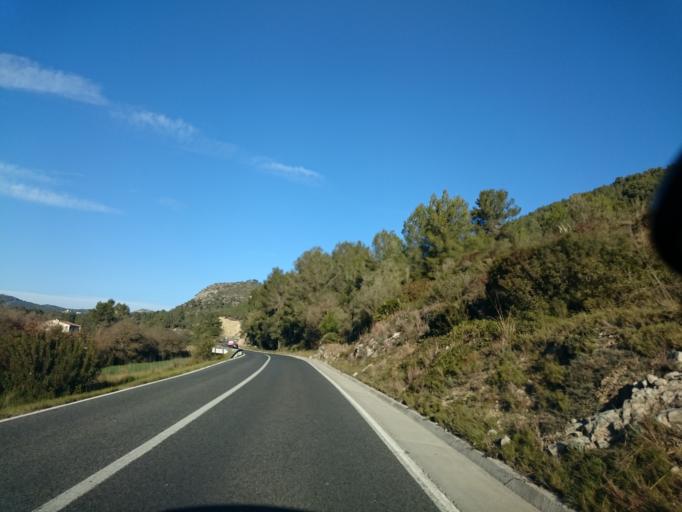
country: ES
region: Catalonia
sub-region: Provincia de Barcelona
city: Sant Pere de Ribes
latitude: 41.2843
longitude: 1.7496
